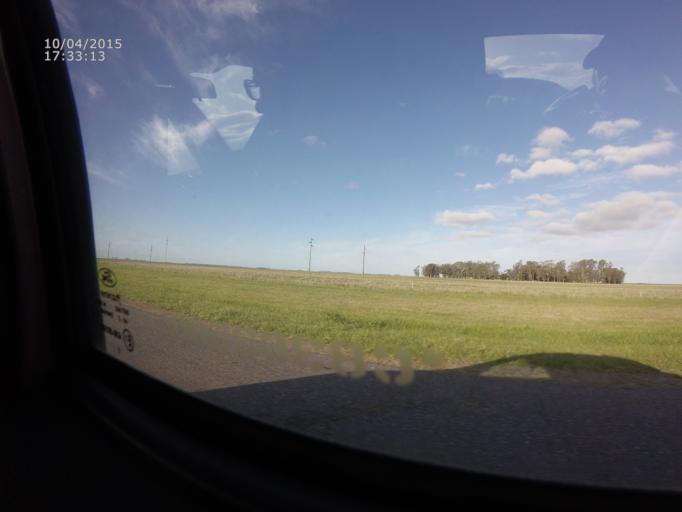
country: AR
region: Buenos Aires
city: Maipu
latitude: -36.9421
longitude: -57.8719
